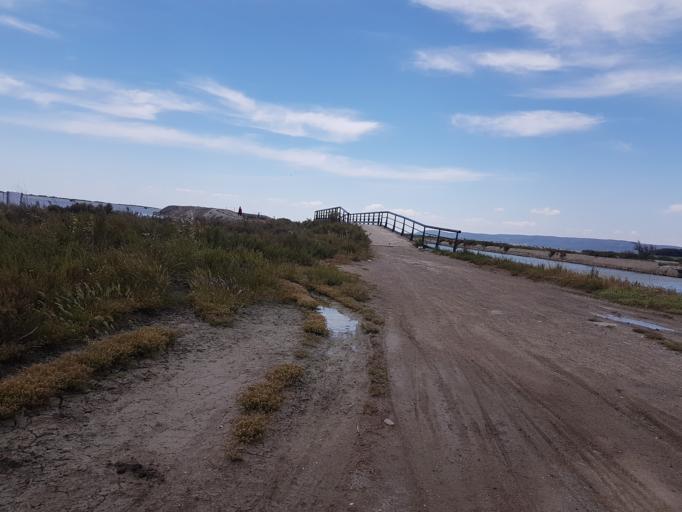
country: FR
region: Languedoc-Roussillon
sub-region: Departement de l'Herault
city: Villeneuve-les-Maguelone
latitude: 43.5089
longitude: 3.8701
